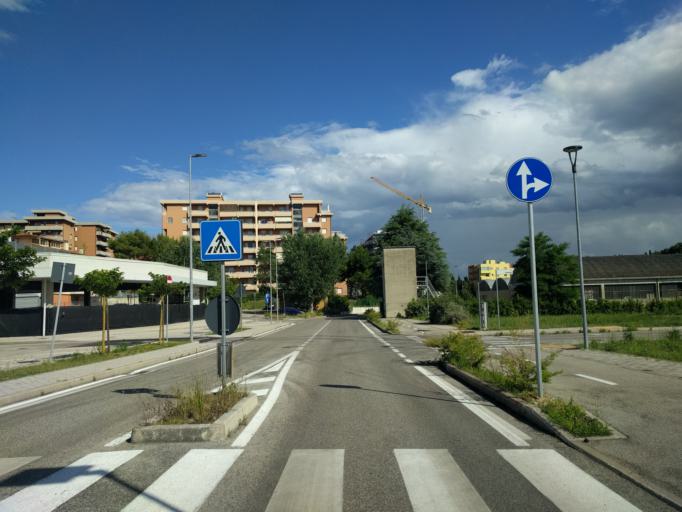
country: IT
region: The Marches
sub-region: Provincia di Pesaro e Urbino
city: Pesaro
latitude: 43.9151
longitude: 12.8618
